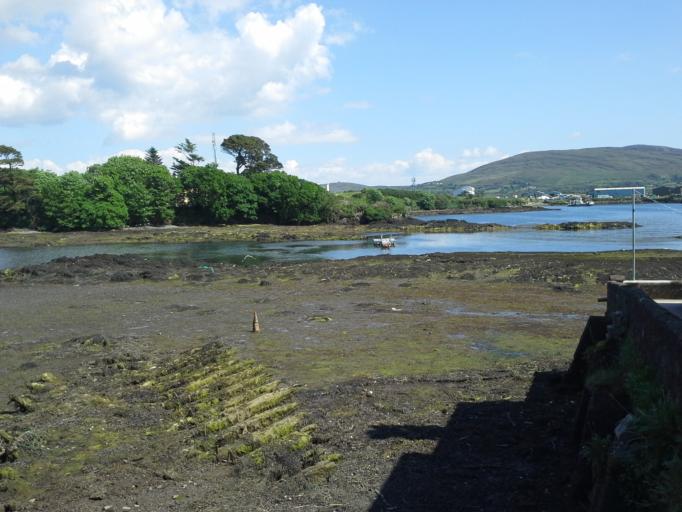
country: IE
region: Munster
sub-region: Ciarrai
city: Kenmare
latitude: 51.6533
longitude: -9.9067
